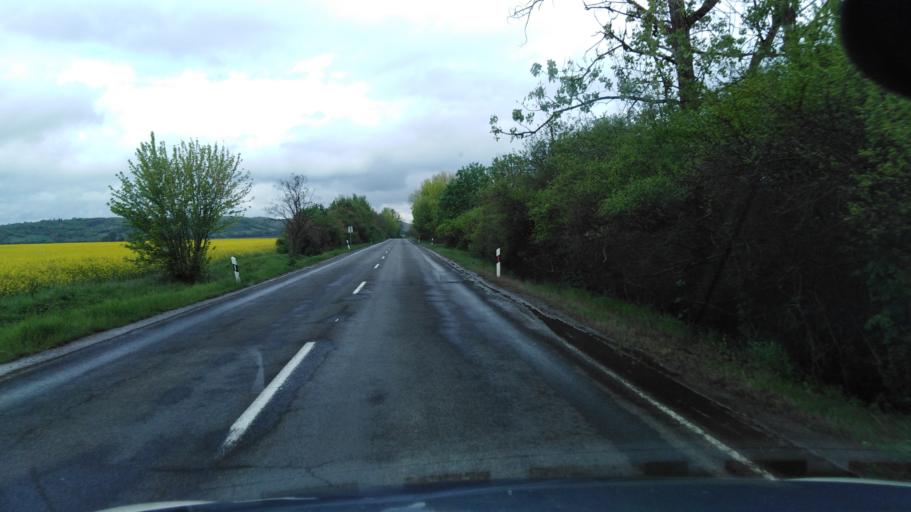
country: HU
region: Nograd
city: Szecseny
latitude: 48.1035
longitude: 19.5415
